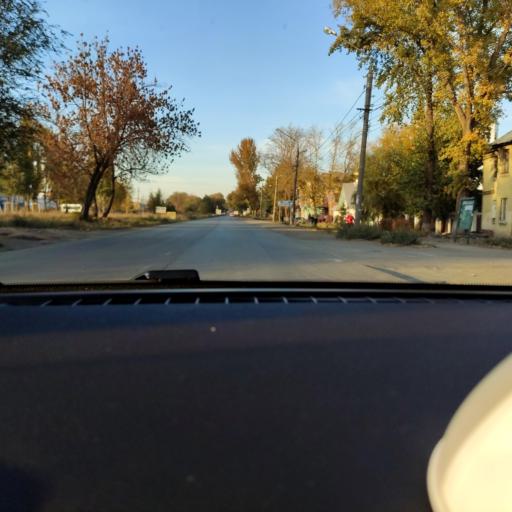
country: RU
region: Samara
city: Petra-Dubrava
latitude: 53.2446
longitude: 50.3092
